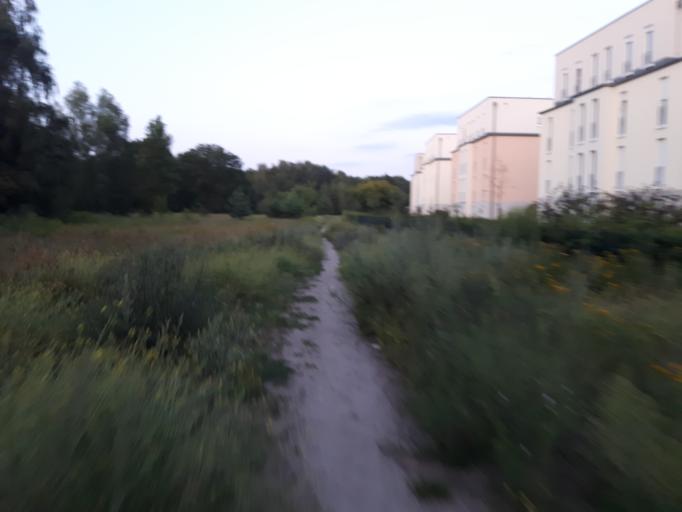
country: DE
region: Berlin
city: Staaken
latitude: 52.5638
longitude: 13.1350
